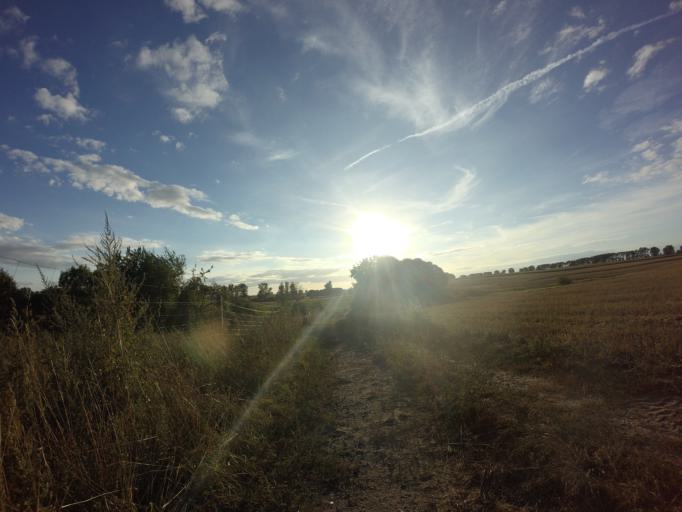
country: PL
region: West Pomeranian Voivodeship
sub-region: Powiat choszczenski
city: Choszczno
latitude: 53.1210
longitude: 15.4043
